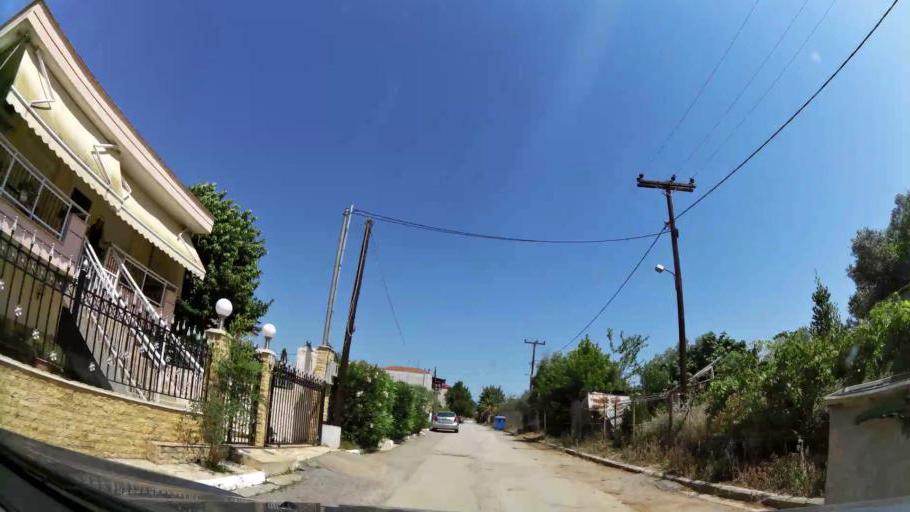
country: GR
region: Central Macedonia
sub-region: Nomos Thessalonikis
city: Agia Triada
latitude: 40.4973
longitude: 22.8368
